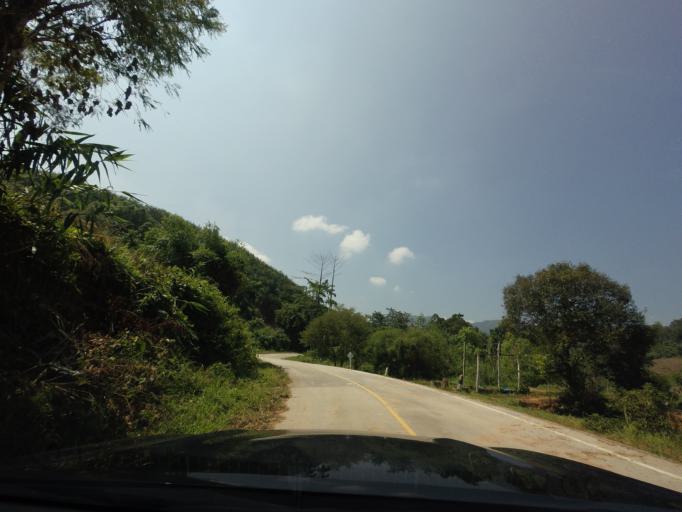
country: TH
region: Loei
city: Na Haeo
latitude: 17.5679
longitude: 100.9533
